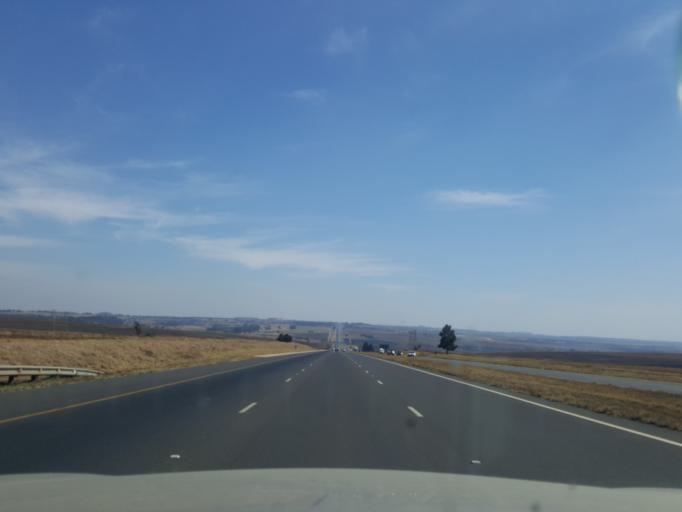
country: ZA
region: Mpumalanga
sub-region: Nkangala District Municipality
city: Middelburg
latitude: -25.8300
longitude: 29.5163
